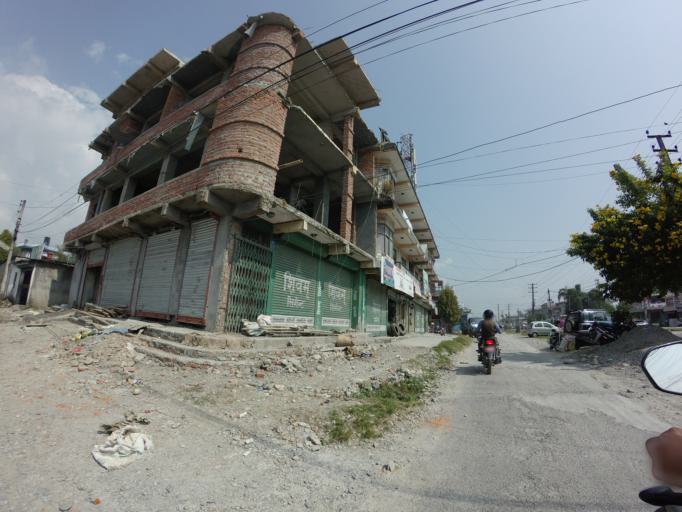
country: NP
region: Western Region
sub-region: Gandaki Zone
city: Pokhara
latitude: 28.2068
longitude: 83.9928
